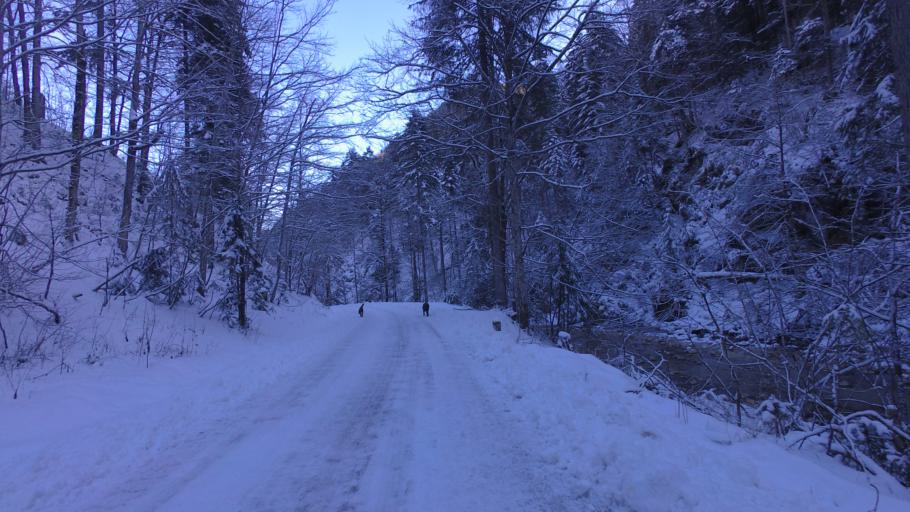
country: DE
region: Bavaria
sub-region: Upper Bavaria
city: Bergen
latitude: 47.7207
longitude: 12.5675
